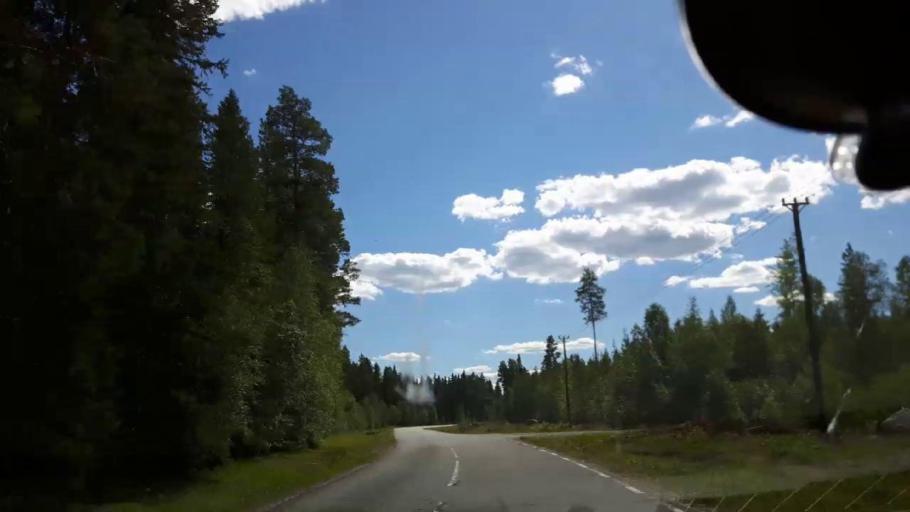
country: SE
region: Jaemtland
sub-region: Ragunda Kommun
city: Hammarstrand
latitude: 62.8859
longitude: 16.2254
